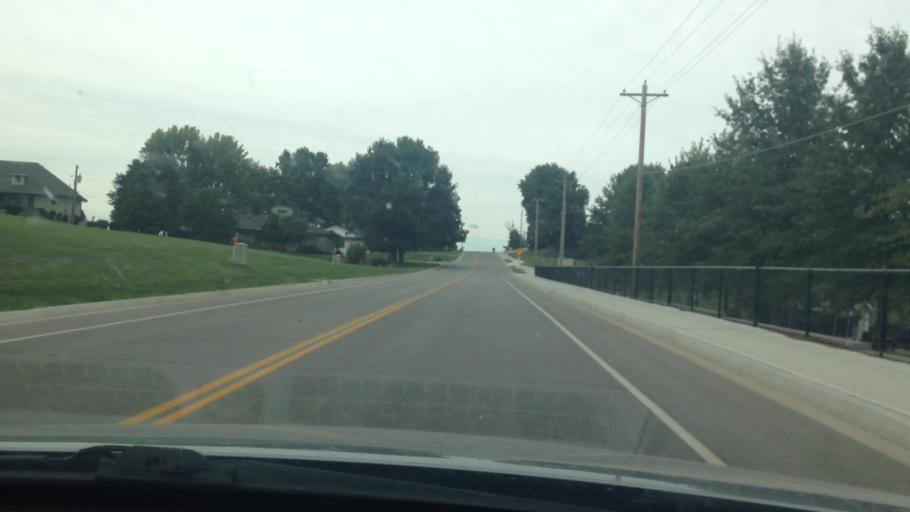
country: US
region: Missouri
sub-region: Platte County
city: Platte City
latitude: 39.3474
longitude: -94.7793
